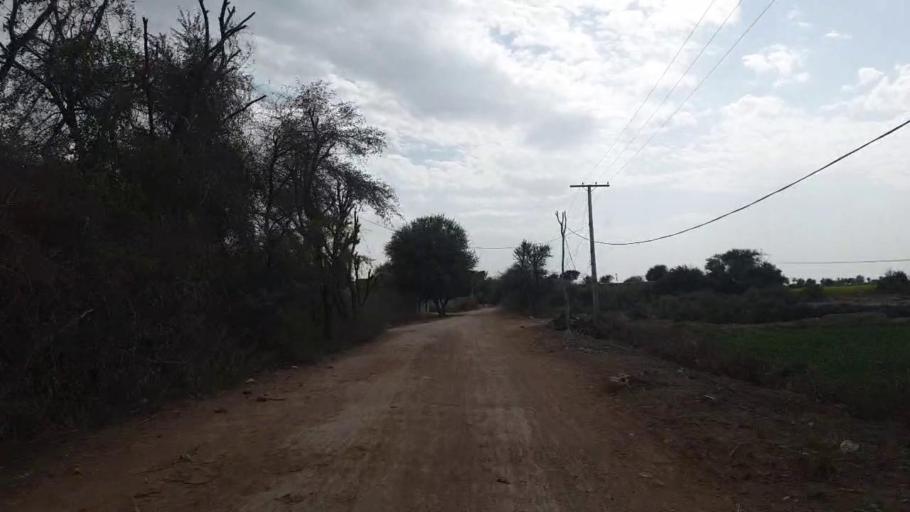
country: PK
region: Sindh
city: Hala
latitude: 25.9311
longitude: 68.4534
